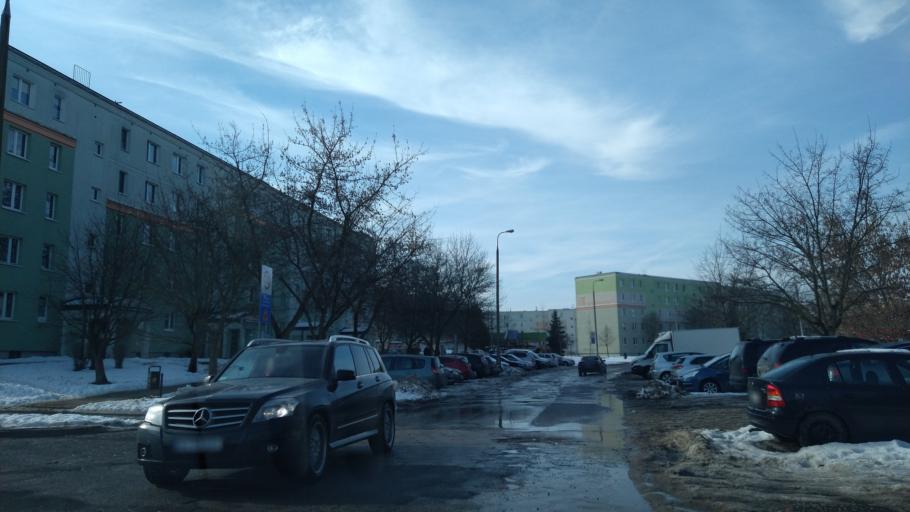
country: PL
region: Warmian-Masurian Voivodeship
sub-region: Powiat olsztynski
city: Olsztyn
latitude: 53.7402
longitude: 20.5178
